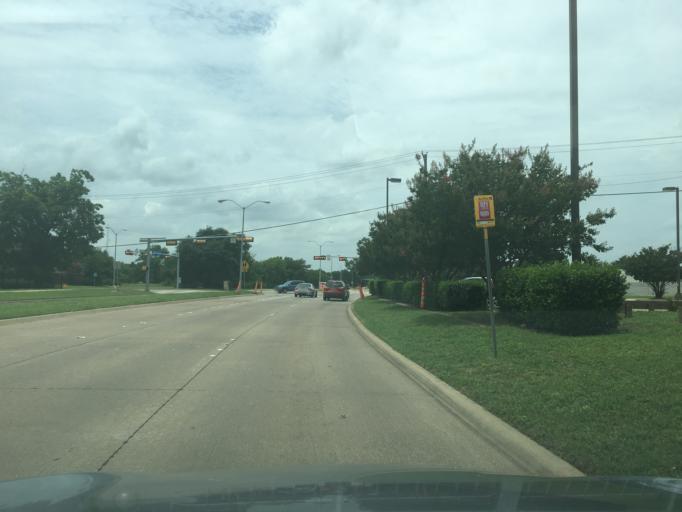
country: US
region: Texas
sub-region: Dallas County
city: Richardson
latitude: 32.9348
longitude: -96.7313
